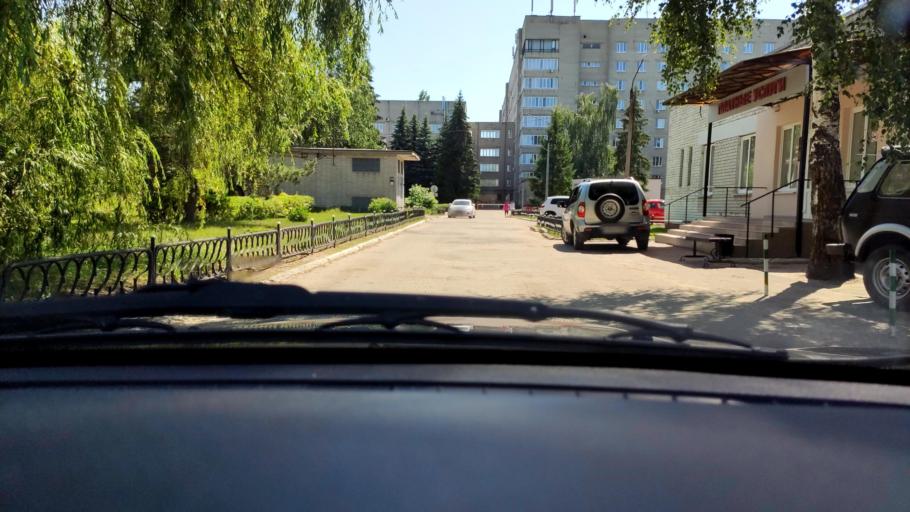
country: RU
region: Voronezj
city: Podgornoye
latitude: 51.7423
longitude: 39.1787
